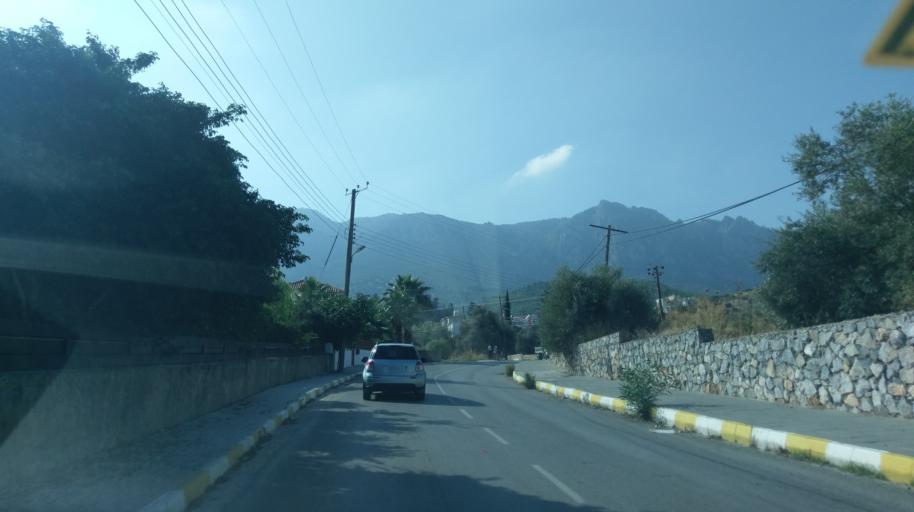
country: CY
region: Keryneia
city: Kyrenia
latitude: 35.3335
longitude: 33.2618
